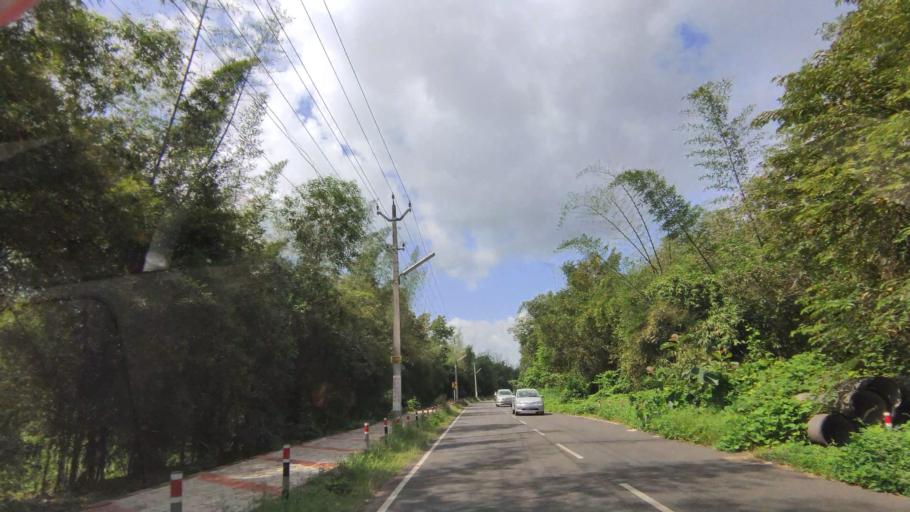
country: IN
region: Kerala
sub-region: Kottayam
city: Kottayam
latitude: 9.5717
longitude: 76.5236
